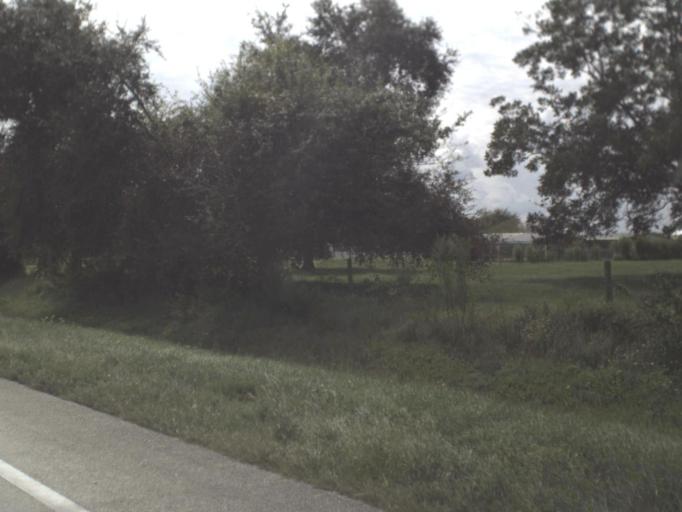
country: US
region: Florida
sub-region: DeSoto County
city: Nocatee
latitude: 27.0838
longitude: -81.7952
